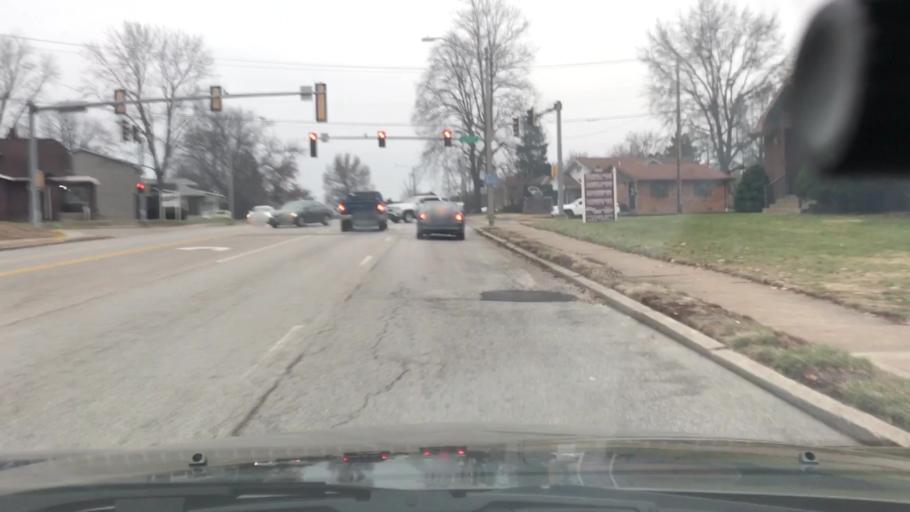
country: US
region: Illinois
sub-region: Saint Clair County
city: Fairview Heights
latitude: 38.5600
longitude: -90.0462
